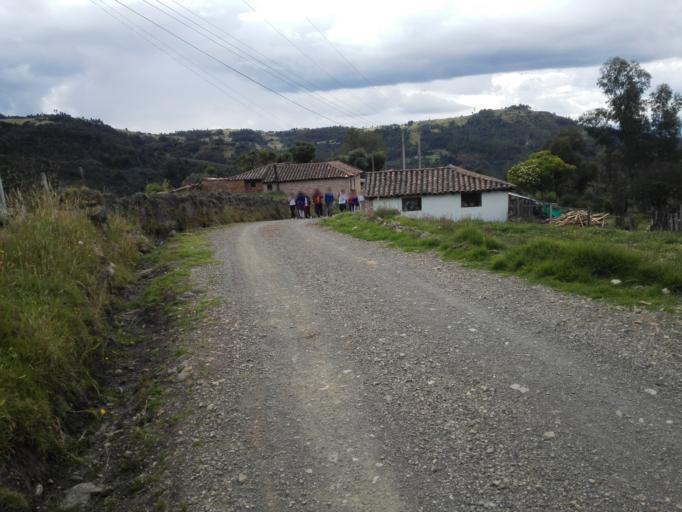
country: CO
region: Boyaca
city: Mongui
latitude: 5.7134
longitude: -72.8462
